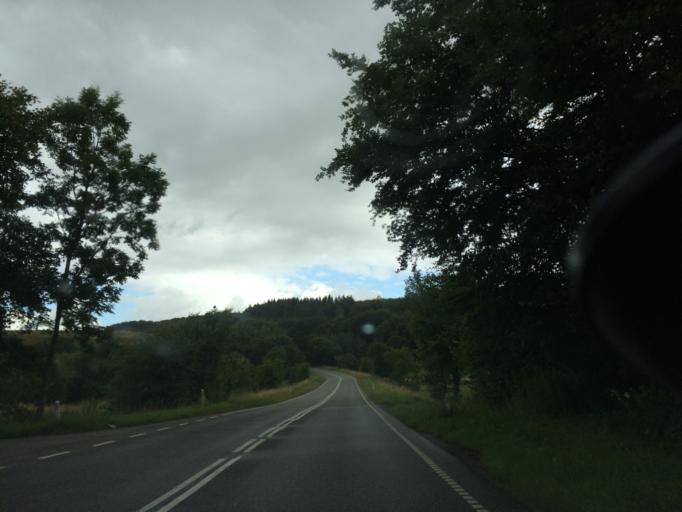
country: DK
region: Central Jutland
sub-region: Skanderborg Kommune
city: Ry
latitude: 56.1639
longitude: 9.8117
